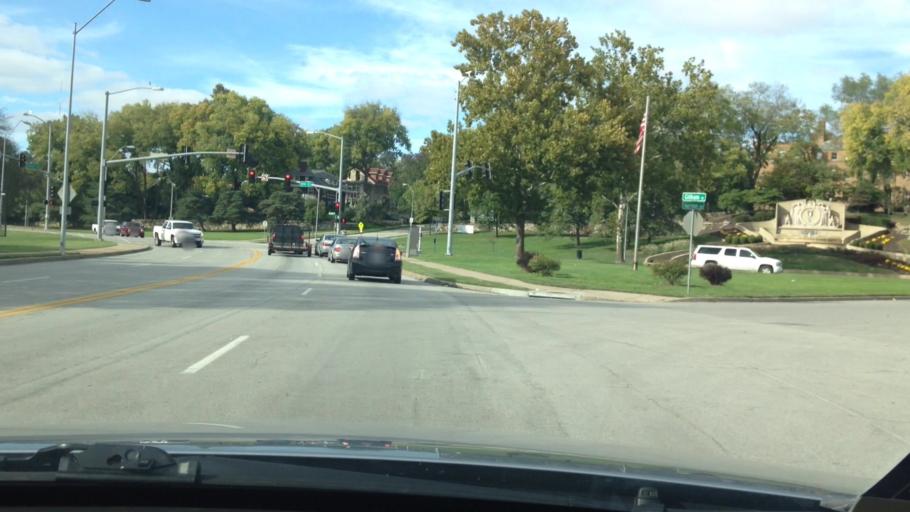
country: US
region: Kansas
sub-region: Johnson County
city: Westwood
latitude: 39.0557
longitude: -94.5796
